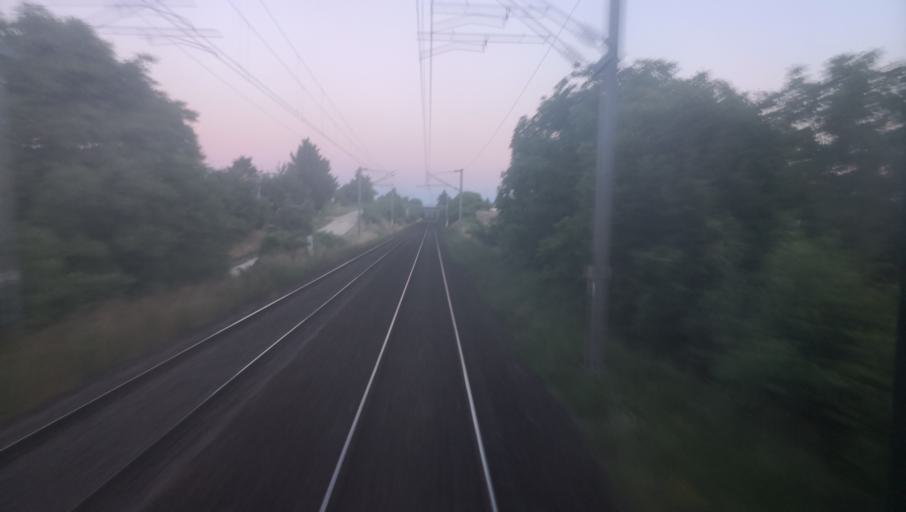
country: FR
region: Centre
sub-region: Departement du Loiret
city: Bonny-sur-Loire
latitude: 47.5657
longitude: 2.8385
